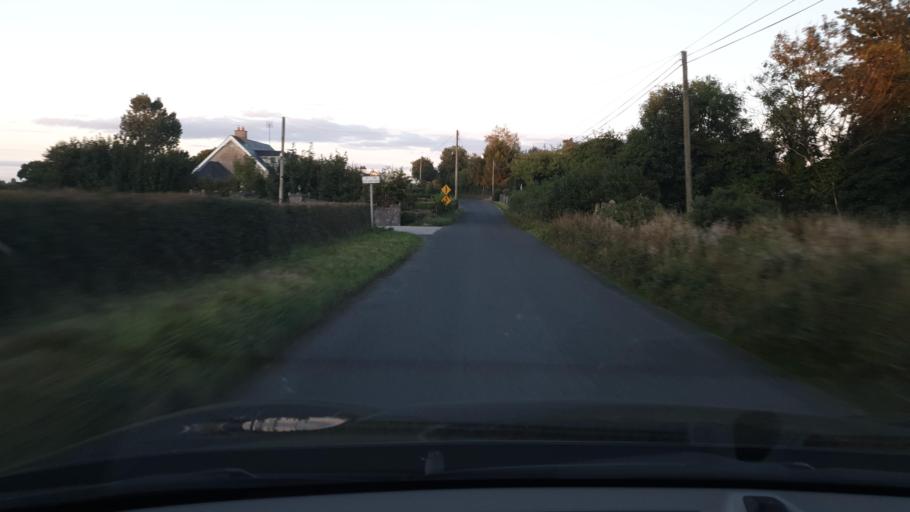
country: IE
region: Leinster
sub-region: Kildare
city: Prosperous
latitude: 53.3229
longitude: -6.7978
